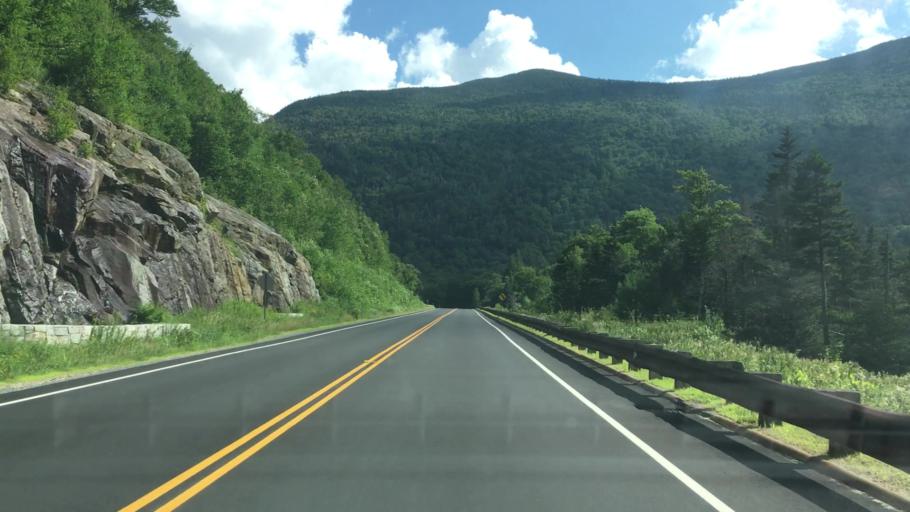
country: US
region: New Hampshire
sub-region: Grafton County
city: Woodstock
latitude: 44.0431
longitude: -71.7918
